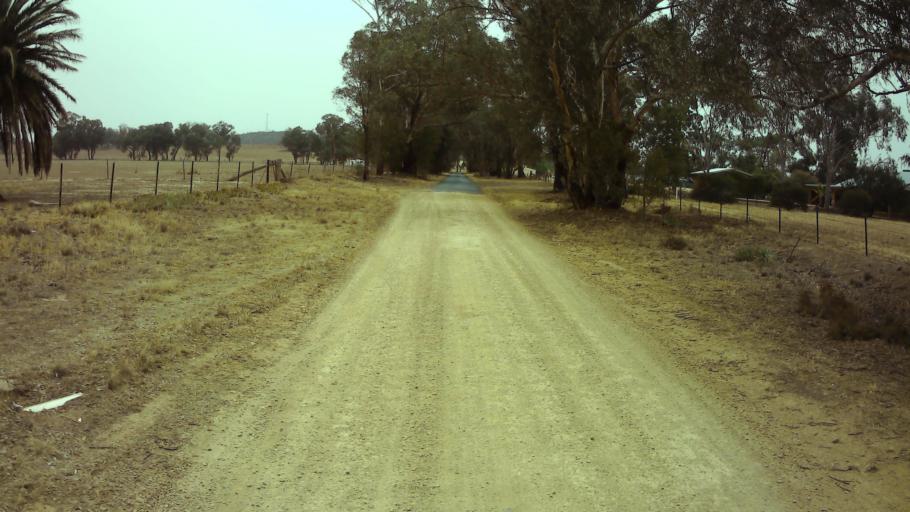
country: AU
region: New South Wales
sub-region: Weddin
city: Grenfell
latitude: -33.8993
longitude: 148.1427
